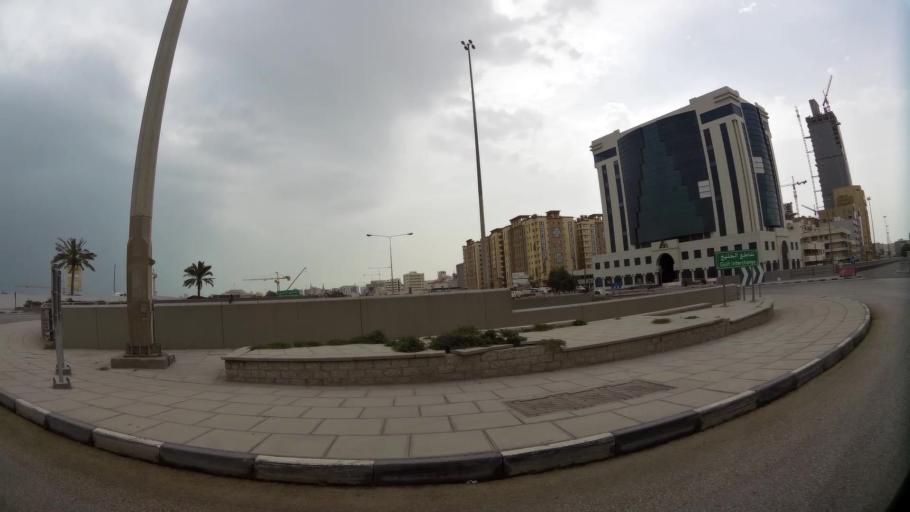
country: QA
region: Baladiyat ad Dawhah
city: Doha
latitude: 25.2895
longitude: 51.5156
